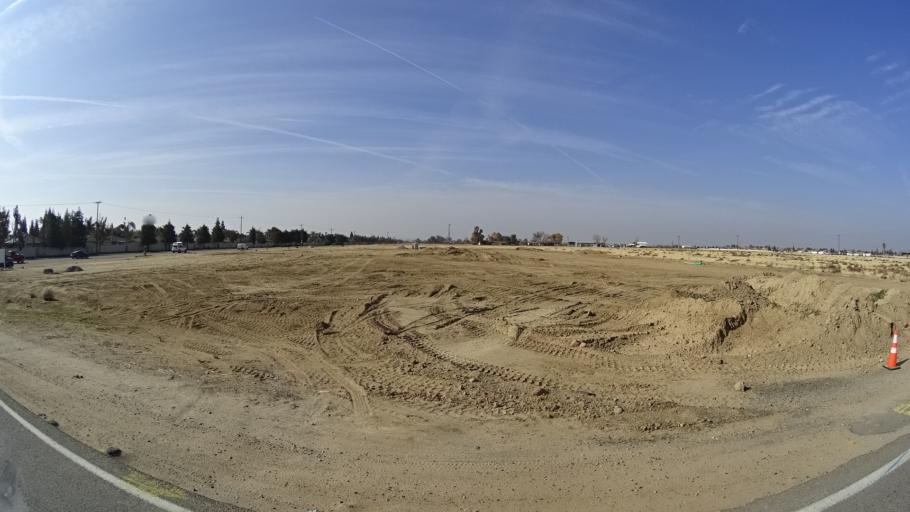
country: US
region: California
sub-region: Kern County
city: Greenacres
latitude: 35.4278
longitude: -119.1099
